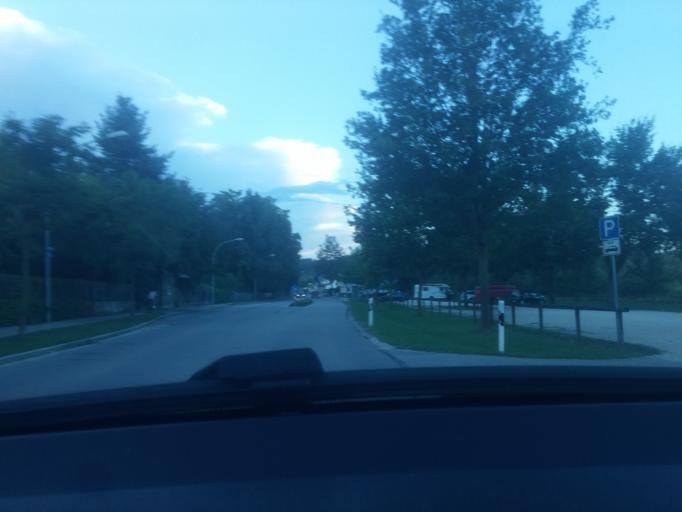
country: DE
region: Bavaria
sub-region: Upper Palatinate
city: Lappersdorf
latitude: 49.0665
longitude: 12.0897
